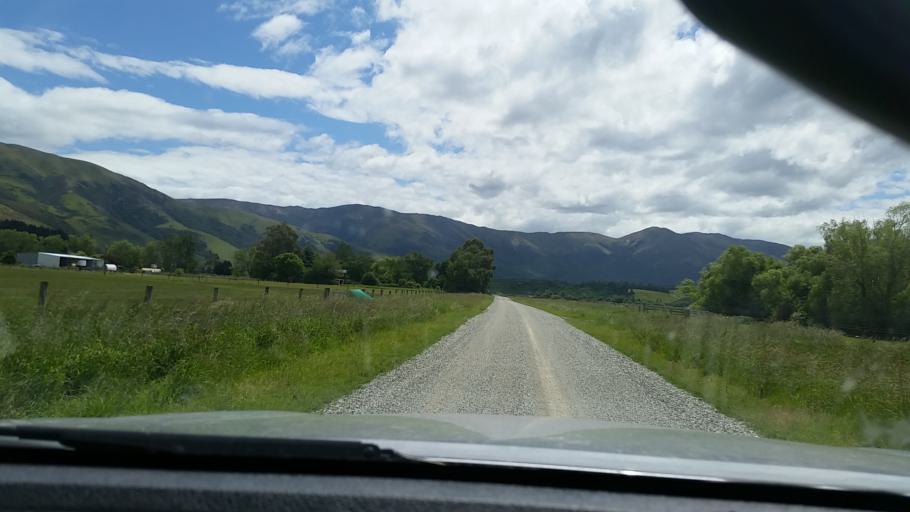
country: NZ
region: Otago
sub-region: Queenstown-Lakes District
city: Kingston
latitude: -45.7028
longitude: 168.6603
